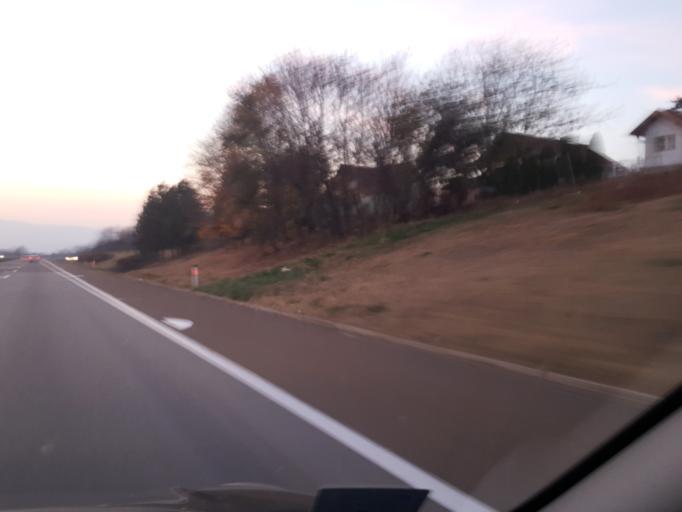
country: RS
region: Central Serbia
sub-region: Pomoravski Okrug
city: Paracin
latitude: 43.8687
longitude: 21.4226
